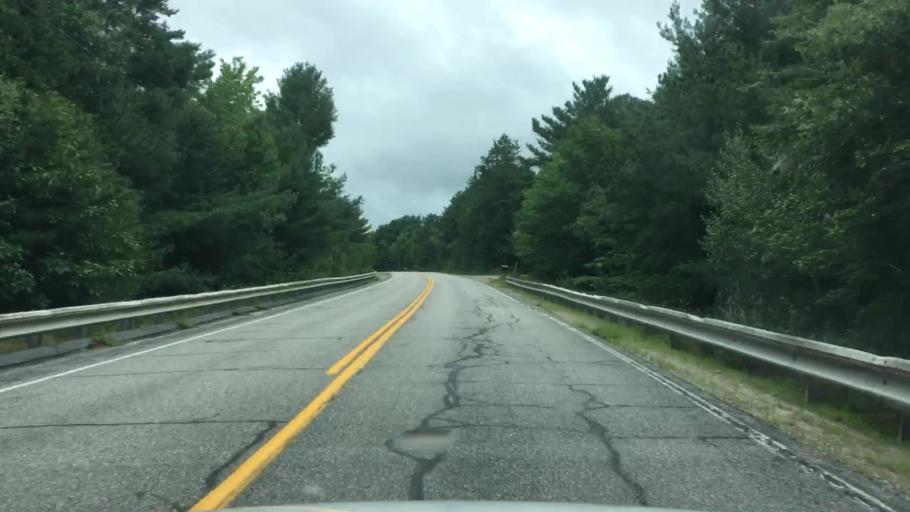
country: US
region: Maine
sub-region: Oxford County
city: Hiram
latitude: 43.9067
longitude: -70.8462
